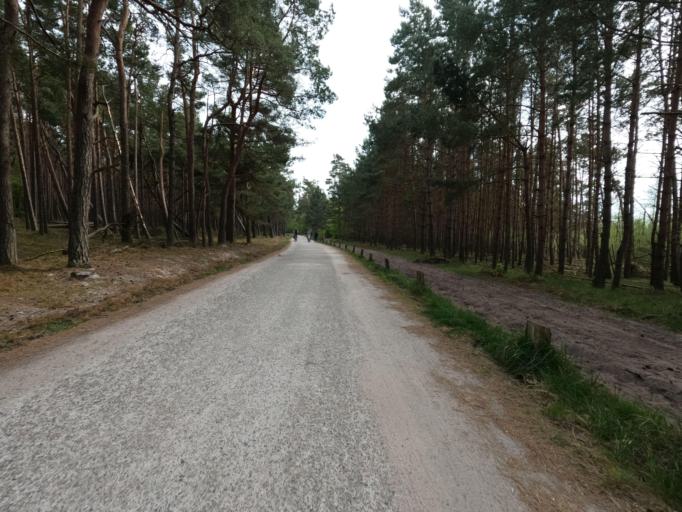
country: DE
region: Mecklenburg-Vorpommern
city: Ostseebad Prerow
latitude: 54.4704
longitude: 12.5056
